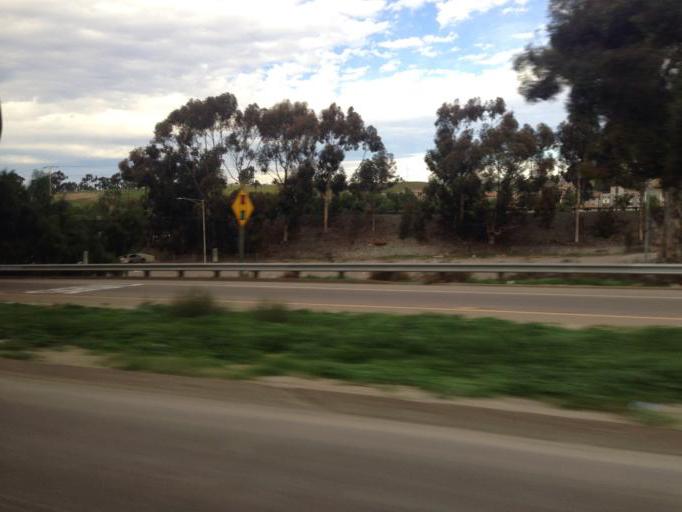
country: US
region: California
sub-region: San Diego County
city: Chula Vista
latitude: 32.6591
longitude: -117.0748
